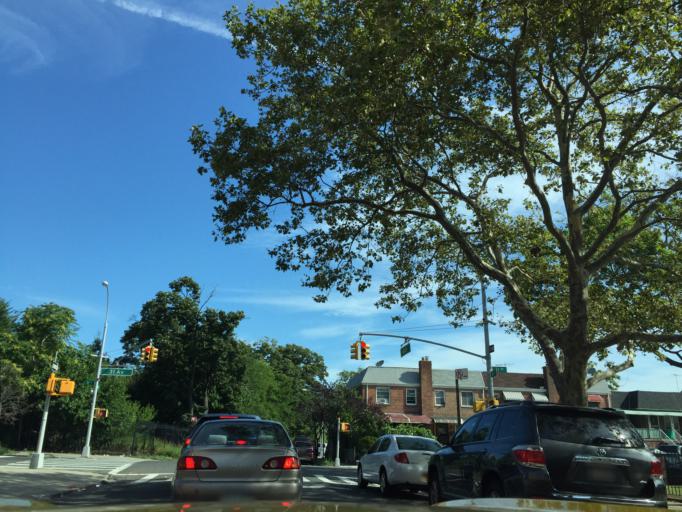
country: US
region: New York
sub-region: Queens County
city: Long Island City
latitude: 40.7575
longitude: -73.8992
